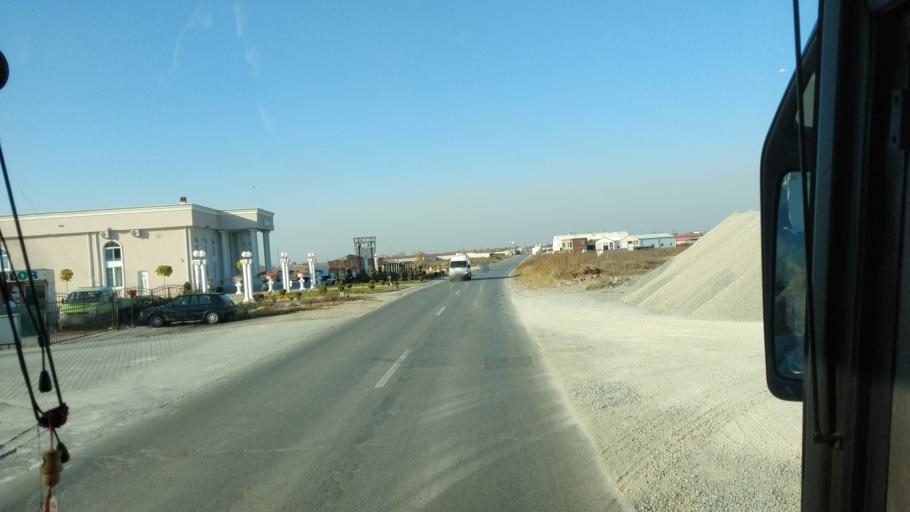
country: XK
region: Pristina
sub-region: Lipjan
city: Lipljan
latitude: 42.5155
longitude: 21.1128
